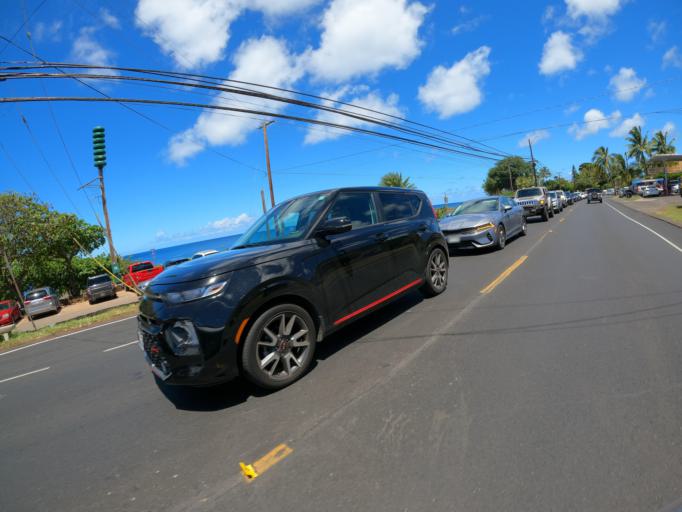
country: US
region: Hawaii
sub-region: Honolulu County
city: Pupukea
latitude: 21.6504
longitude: -158.0619
